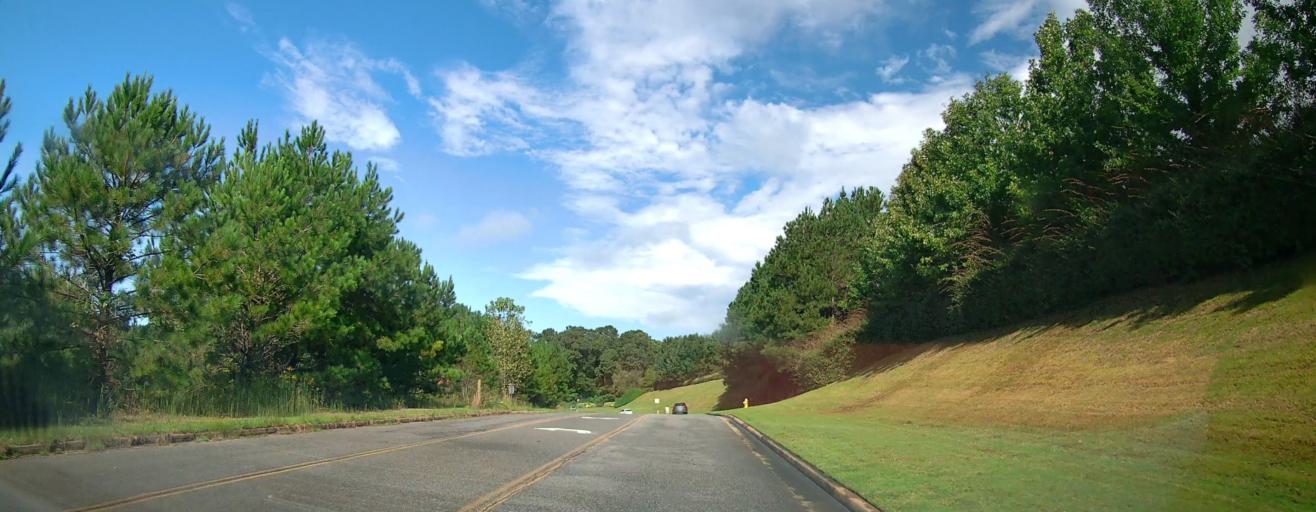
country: US
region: Georgia
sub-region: Bibb County
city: Macon
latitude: 32.9237
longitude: -83.7157
